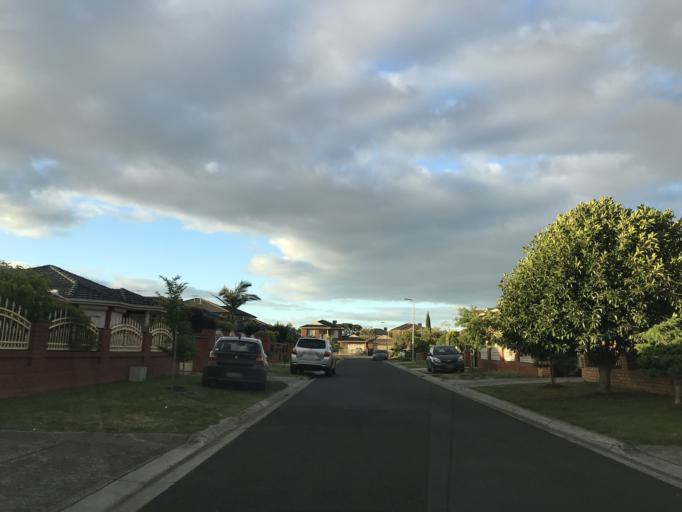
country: AU
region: Victoria
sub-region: Brimbank
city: Sunshine West
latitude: -37.7977
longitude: 144.8002
